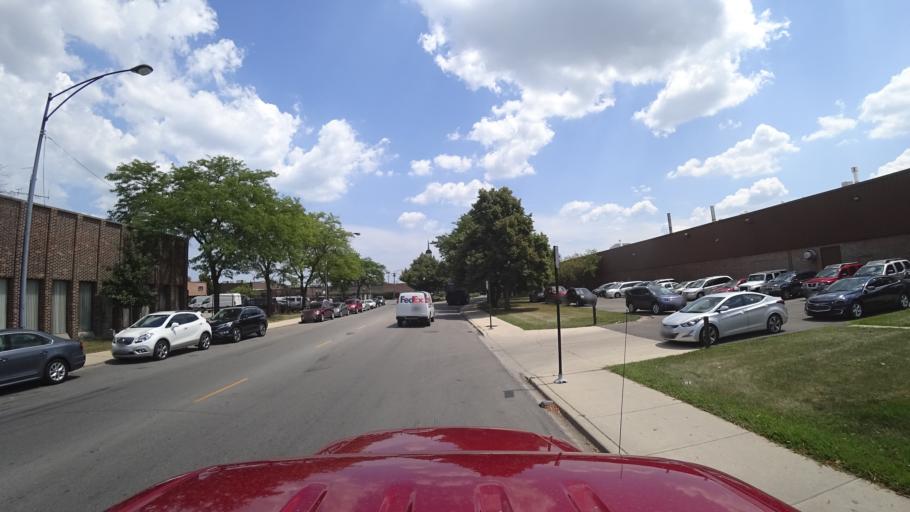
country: US
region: Illinois
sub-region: Cook County
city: Chicago
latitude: 41.8187
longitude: -87.6501
